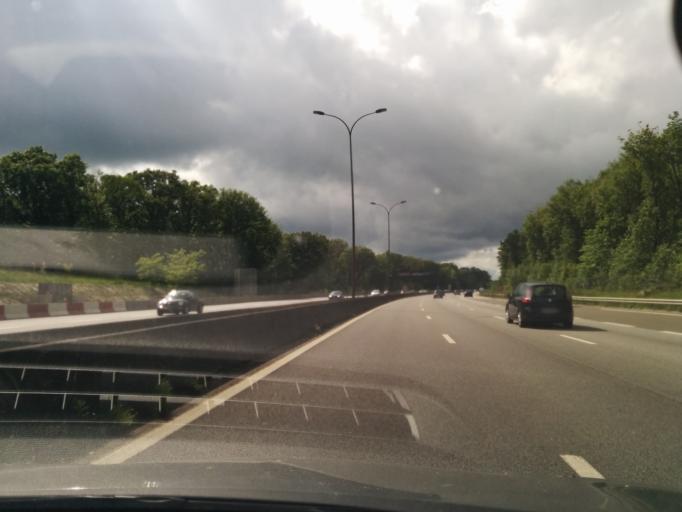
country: FR
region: Ile-de-France
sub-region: Departement des Hauts-de-Seine
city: Vaucresson
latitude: 48.8320
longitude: 2.1418
